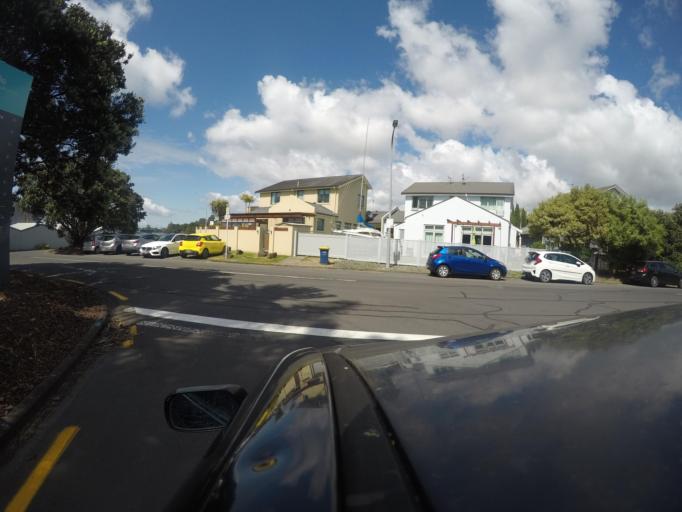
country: NZ
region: Auckland
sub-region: Auckland
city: Rosebank
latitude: -36.8109
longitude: 174.6443
